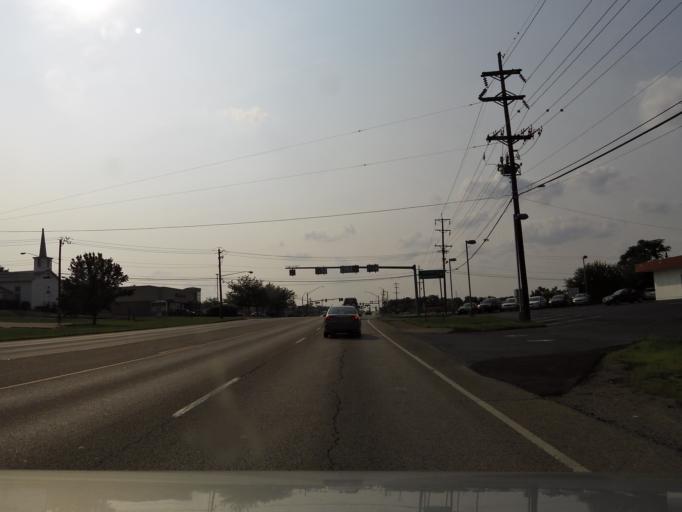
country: US
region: Ohio
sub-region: Hamilton County
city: Forest Park
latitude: 39.3221
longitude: -84.5028
